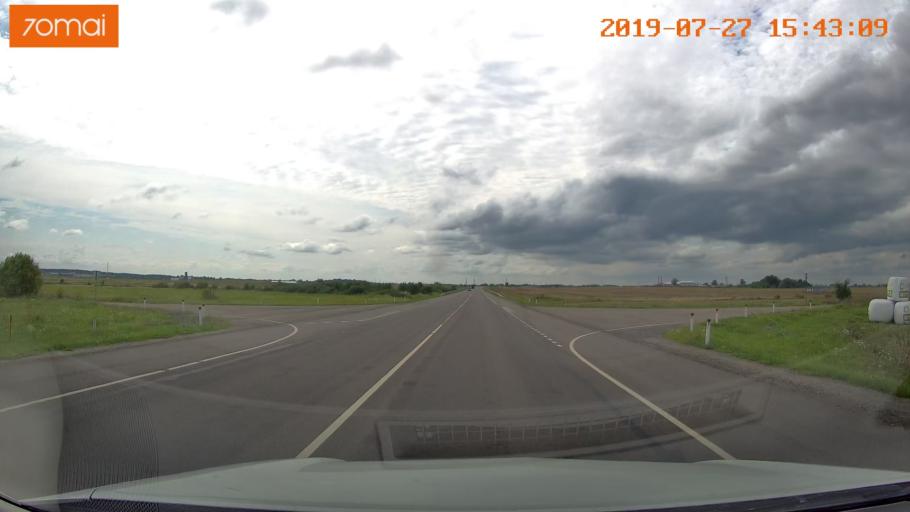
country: RU
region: Kaliningrad
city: Gusev
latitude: 54.6161
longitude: 22.2007
